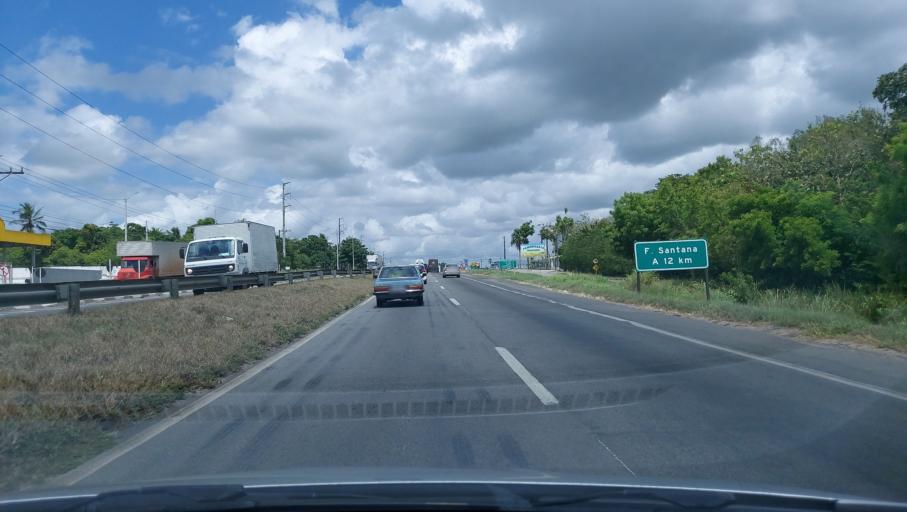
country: BR
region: Bahia
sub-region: Conceicao Do Jacuipe
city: Conceicao do Jacuipe
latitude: -12.3354
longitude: -38.8520
